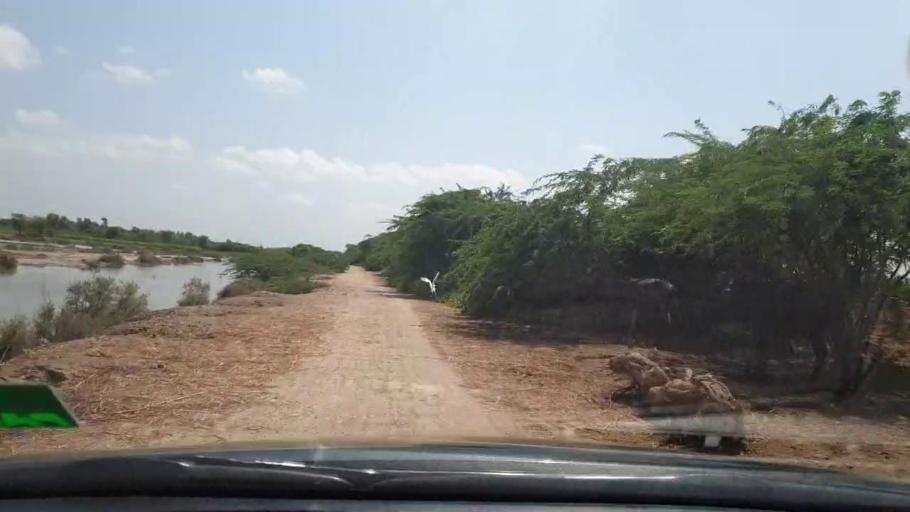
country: PK
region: Sindh
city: Tando Bago
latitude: 24.8538
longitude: 69.0899
